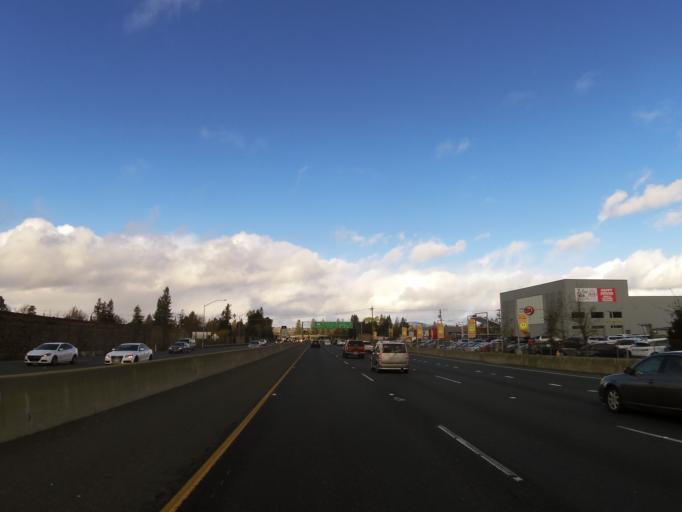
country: US
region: California
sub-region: Sonoma County
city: Roseland
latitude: 38.4255
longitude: -122.7147
